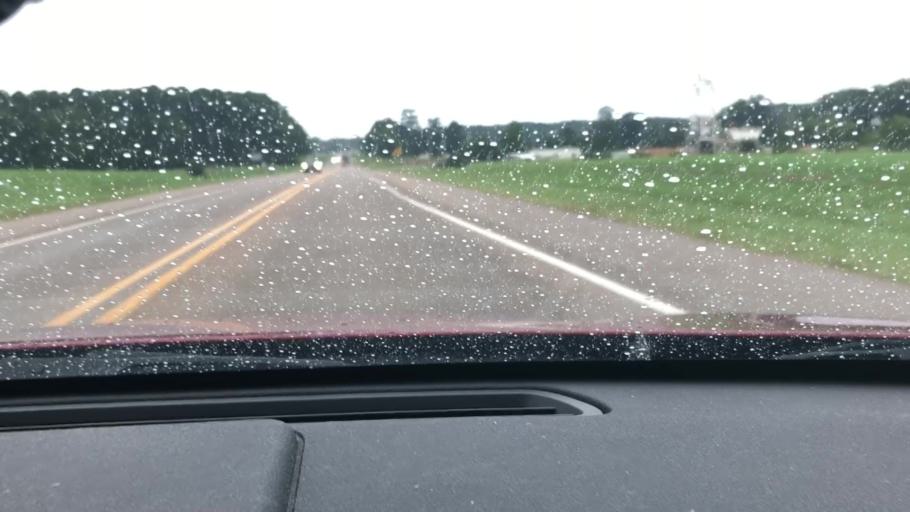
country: US
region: Arkansas
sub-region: Columbia County
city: Magnolia
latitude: 33.2973
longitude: -93.2381
